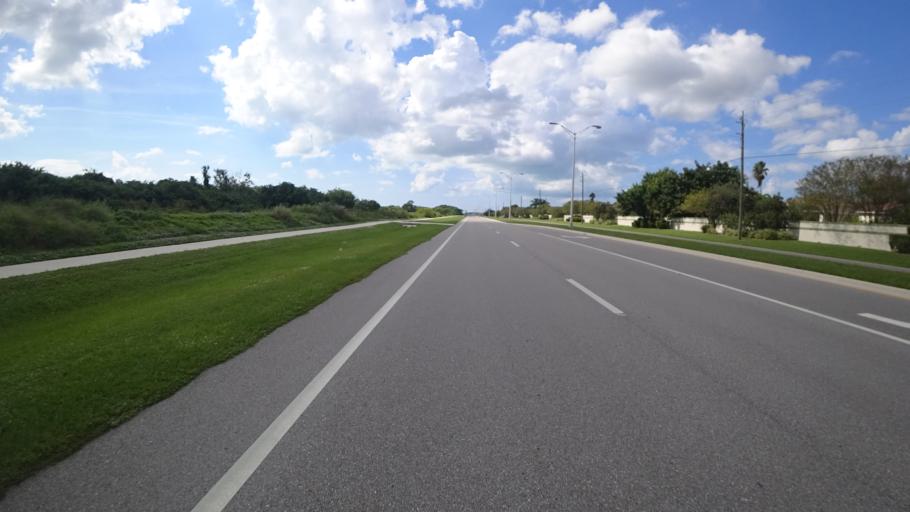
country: US
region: Florida
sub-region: Manatee County
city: Bayshore Gardens
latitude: 27.4477
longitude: -82.6161
